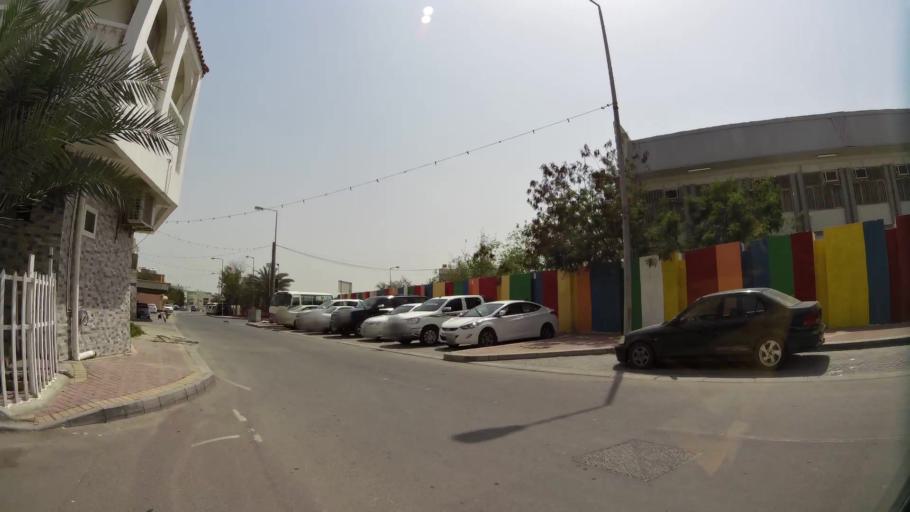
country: BH
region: Manama
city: Jidd Hafs
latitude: 26.2302
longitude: 50.4777
